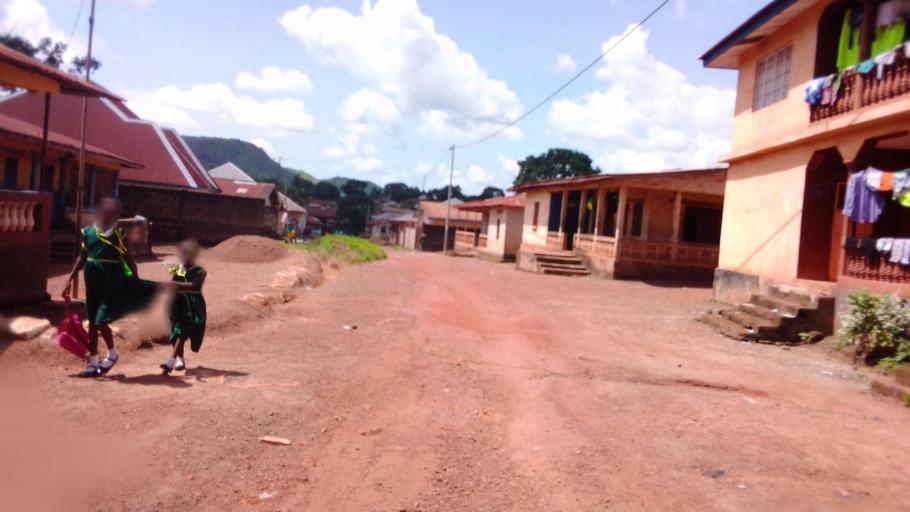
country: SL
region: Northern Province
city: Makeni
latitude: 8.8871
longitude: -12.0352
